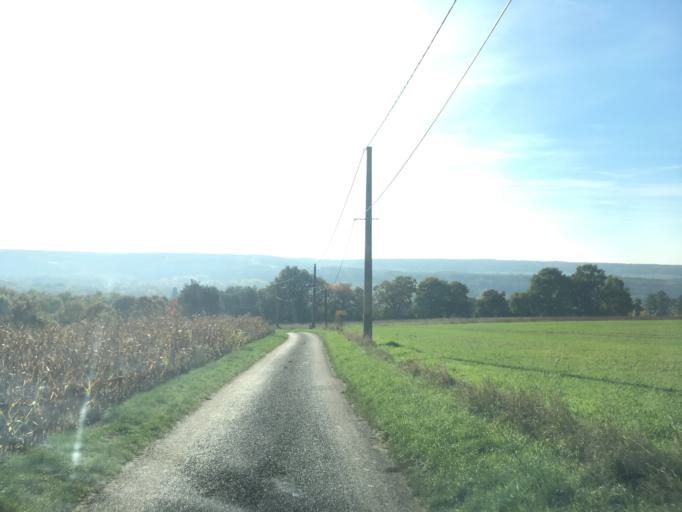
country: FR
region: Haute-Normandie
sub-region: Departement de l'Eure
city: Heudreville-sur-Eure
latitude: 49.1375
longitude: 1.2147
